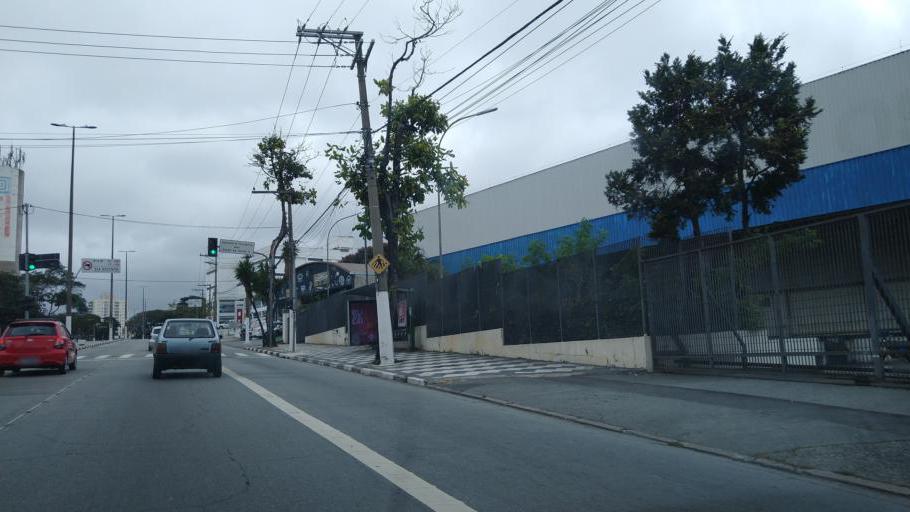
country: BR
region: Sao Paulo
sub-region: Osasco
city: Osasco
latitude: -23.5268
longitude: -46.7887
